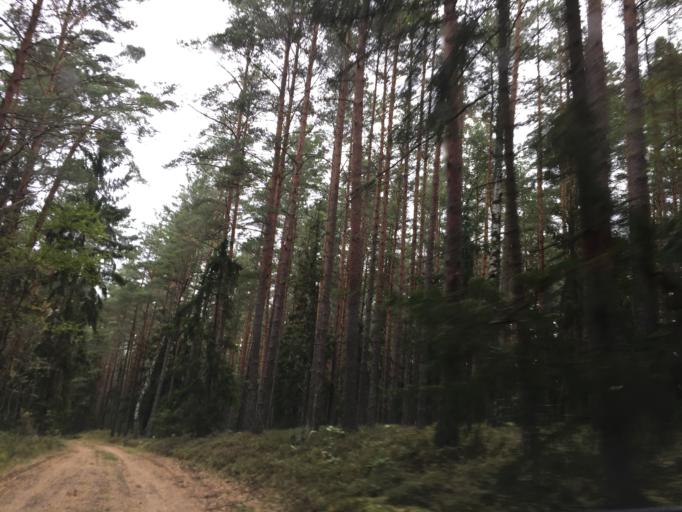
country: LV
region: Salacgrivas
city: Salacgriva
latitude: 57.7063
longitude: 24.3544
